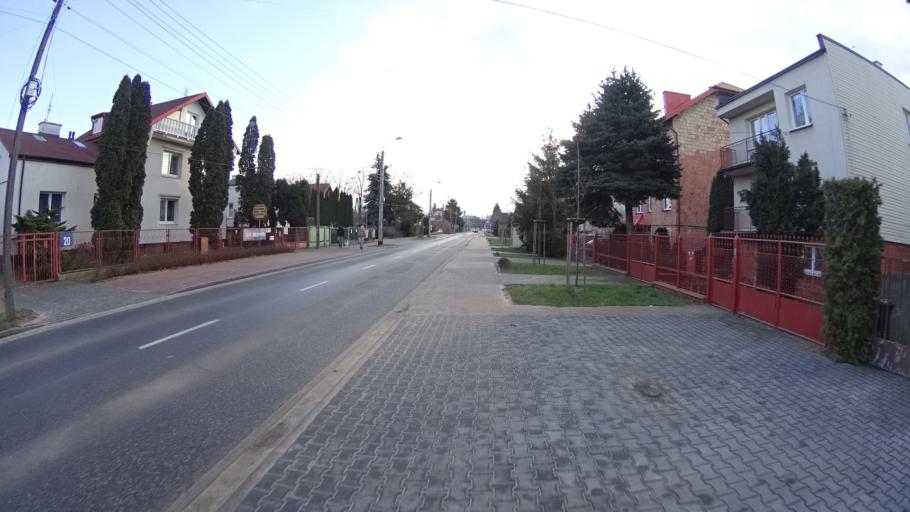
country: PL
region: Masovian Voivodeship
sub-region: Powiat warszawski zachodni
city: Ozarow Mazowiecki
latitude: 52.2171
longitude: 20.7999
